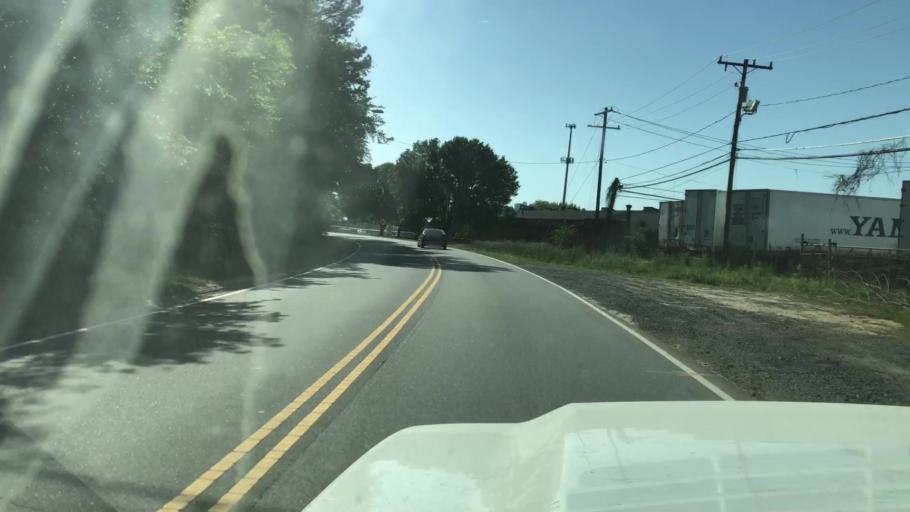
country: US
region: North Carolina
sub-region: Mecklenburg County
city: Charlotte
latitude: 35.2819
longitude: -80.9041
